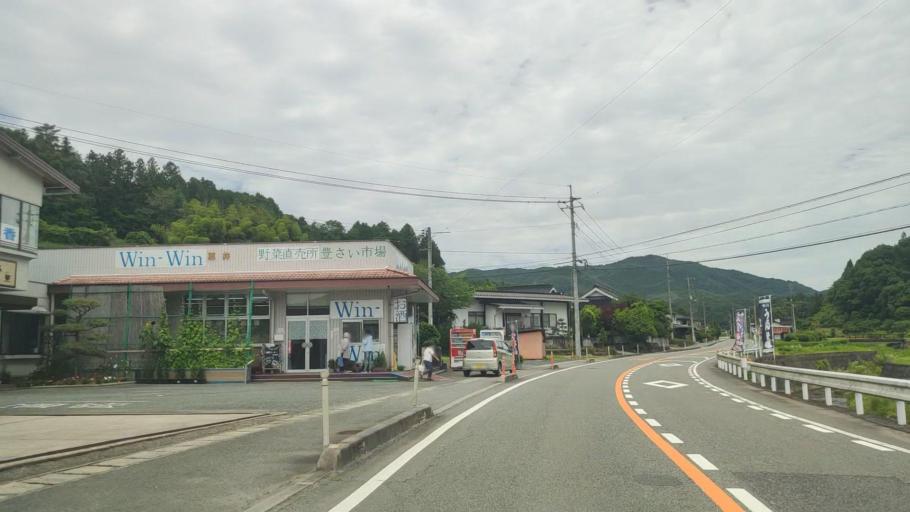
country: JP
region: Okayama
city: Tsuyama
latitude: 35.0763
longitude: 134.2454
